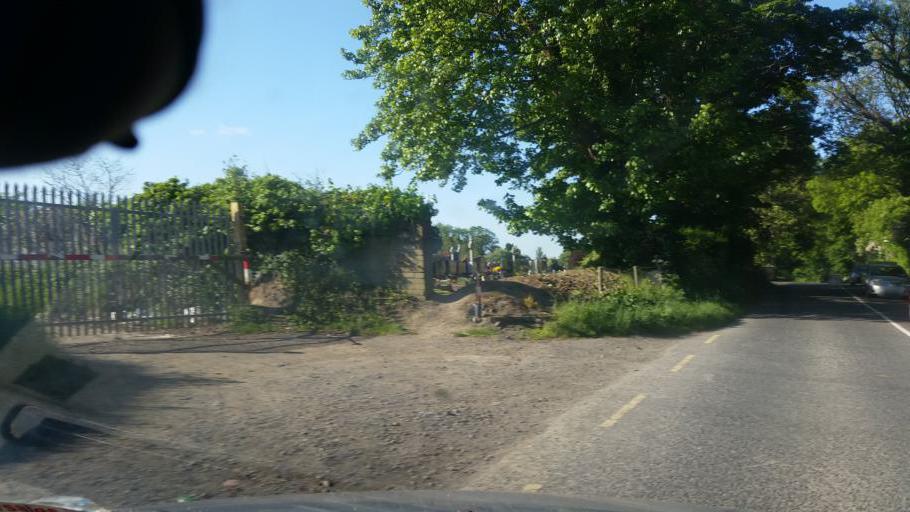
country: IE
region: Leinster
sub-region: Fingal County
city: Blanchardstown
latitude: 53.4130
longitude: -6.3876
